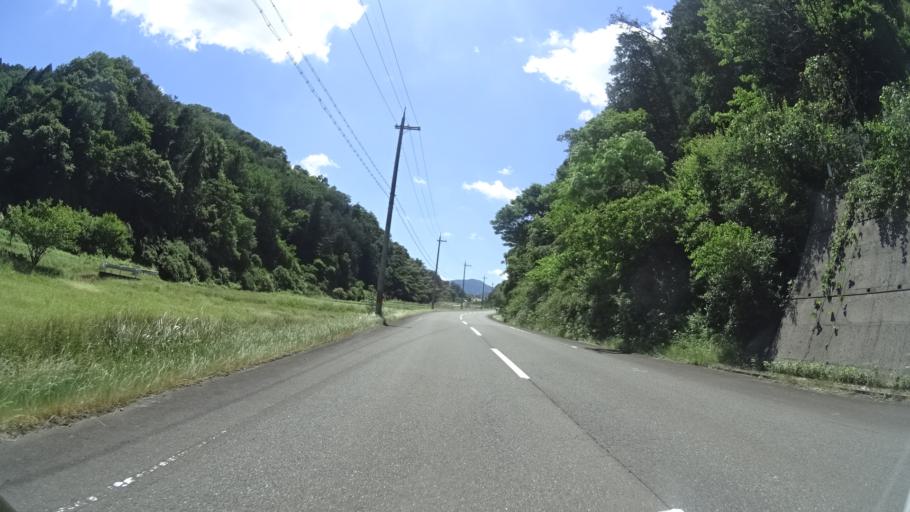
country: JP
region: Kyoto
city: Miyazu
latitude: 35.4202
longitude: 135.1771
